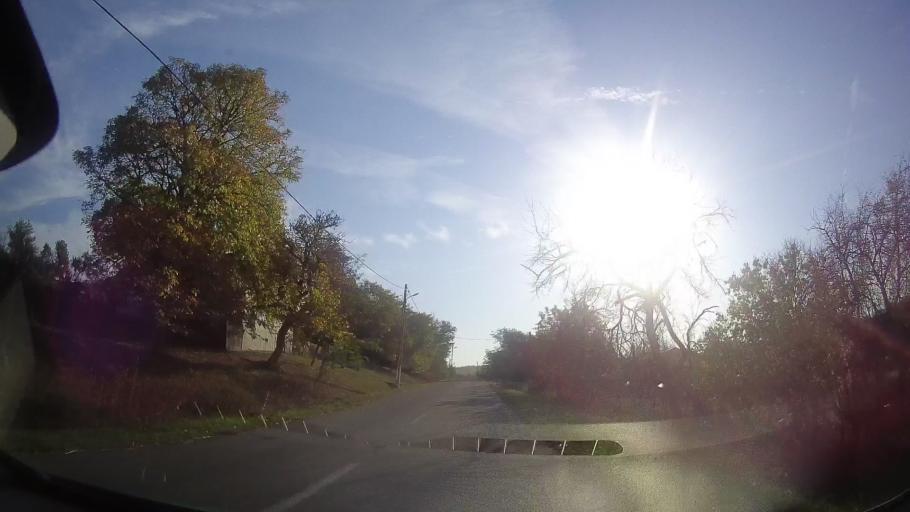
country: RO
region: Timis
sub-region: Comuna Bogda
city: Bogda
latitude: 45.9742
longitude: 21.5952
